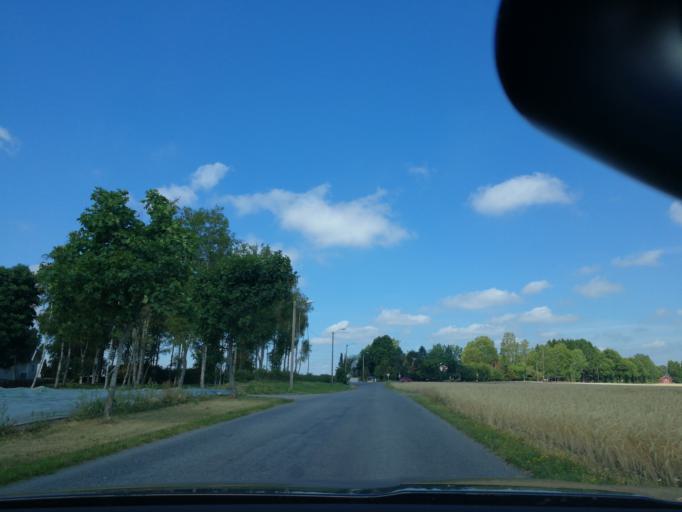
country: NO
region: Vestfold
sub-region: Sandefjord
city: Sandefjord
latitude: 59.1547
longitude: 10.2010
